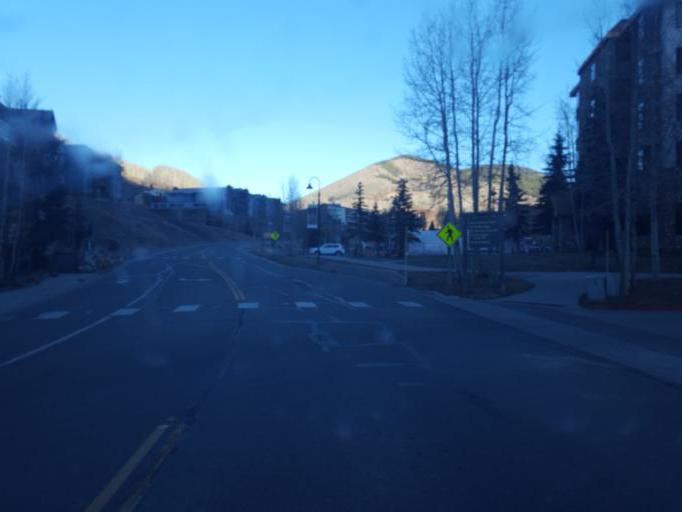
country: US
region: Colorado
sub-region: Gunnison County
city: Crested Butte
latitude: 38.9004
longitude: -106.9675
